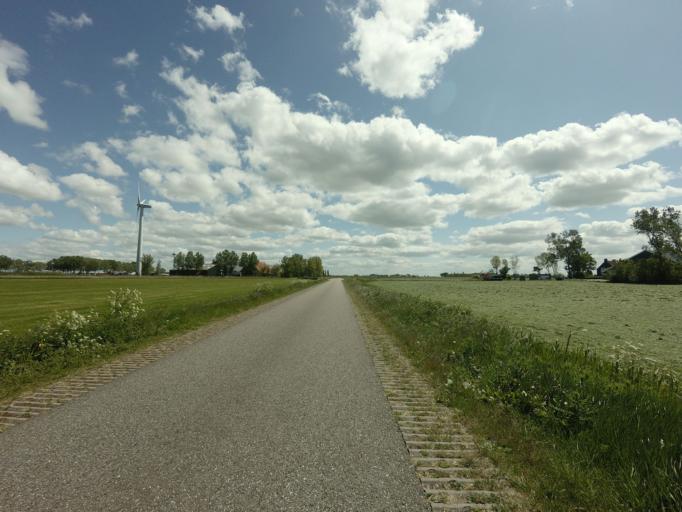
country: NL
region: Friesland
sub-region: Sudwest Fryslan
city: Makkum
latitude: 53.0922
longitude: 5.4107
